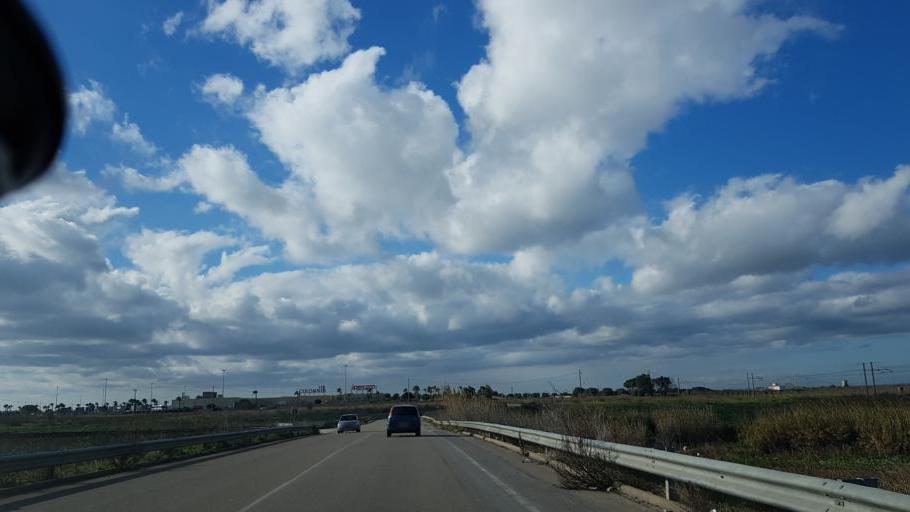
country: IT
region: Apulia
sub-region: Provincia di Brindisi
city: Brindisi
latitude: 40.6231
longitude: 17.9075
